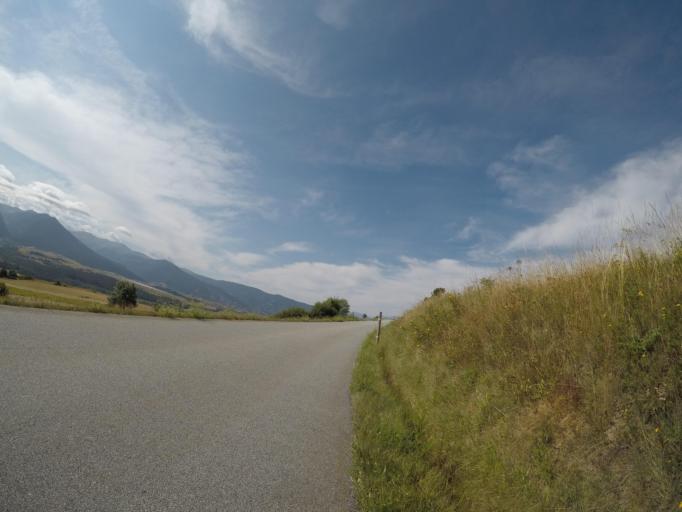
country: ES
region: Catalonia
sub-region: Provincia de Girona
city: Llivia
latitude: 42.4969
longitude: 2.0542
